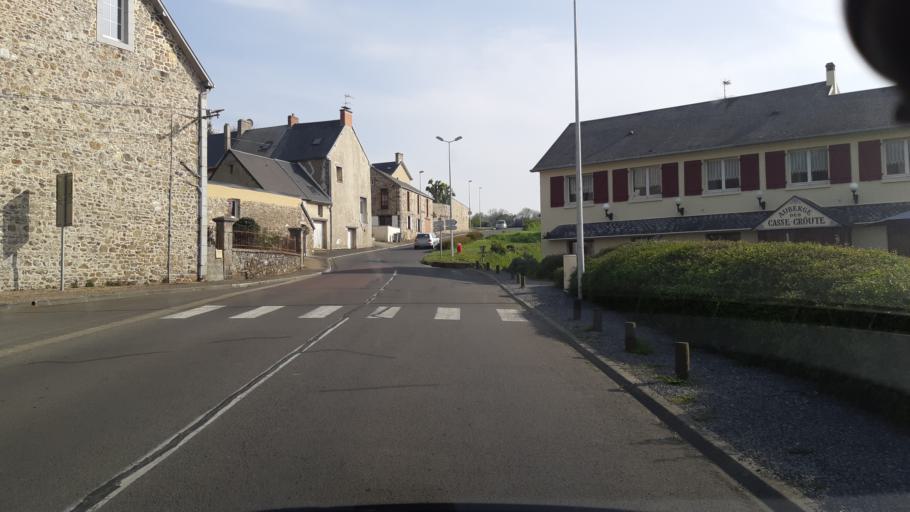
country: FR
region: Lower Normandy
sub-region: Departement de la Manche
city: Donville-les-Bains
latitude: 48.8651
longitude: -1.5562
